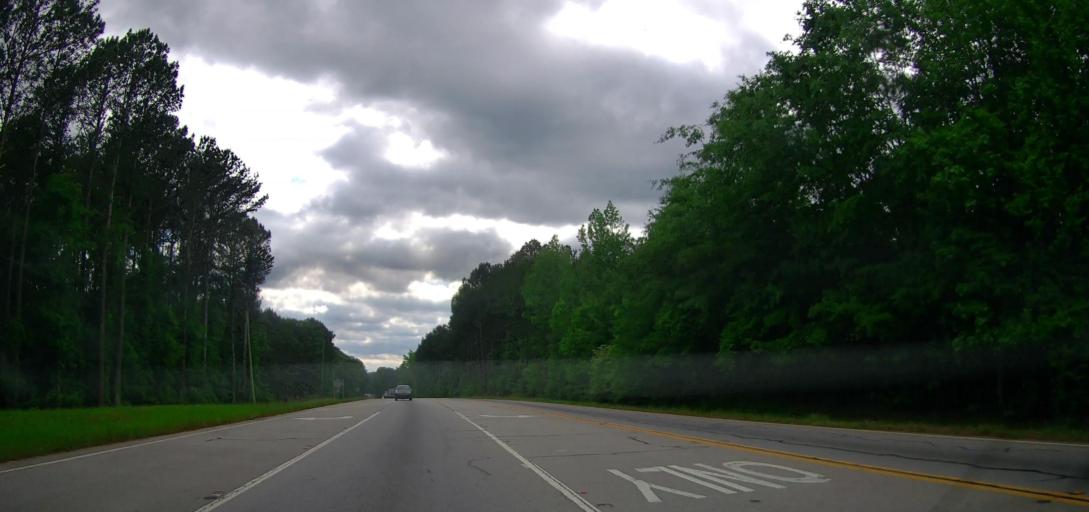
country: US
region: Georgia
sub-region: Walton County
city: Walnut Grove
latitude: 33.7260
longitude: -83.9025
